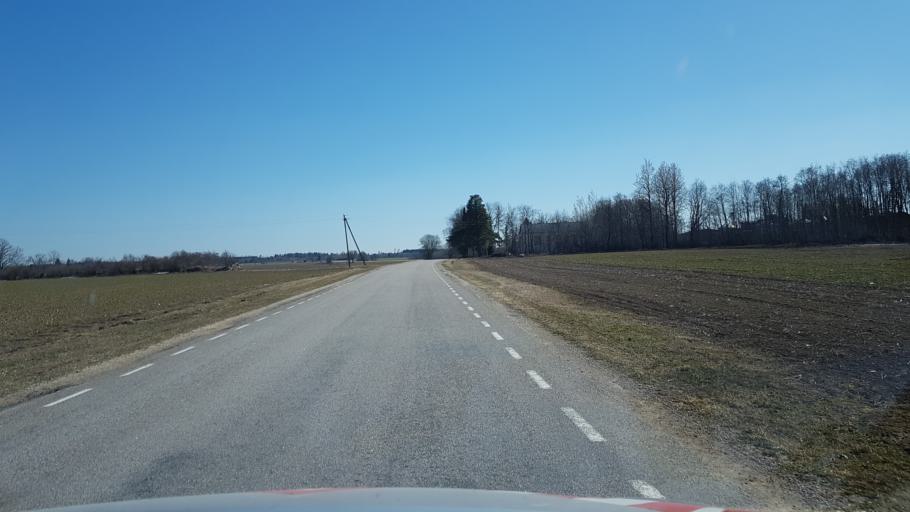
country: EE
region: Laeaene-Virumaa
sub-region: Vaeike-Maarja vald
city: Vaike-Maarja
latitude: 59.1112
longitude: 26.3744
